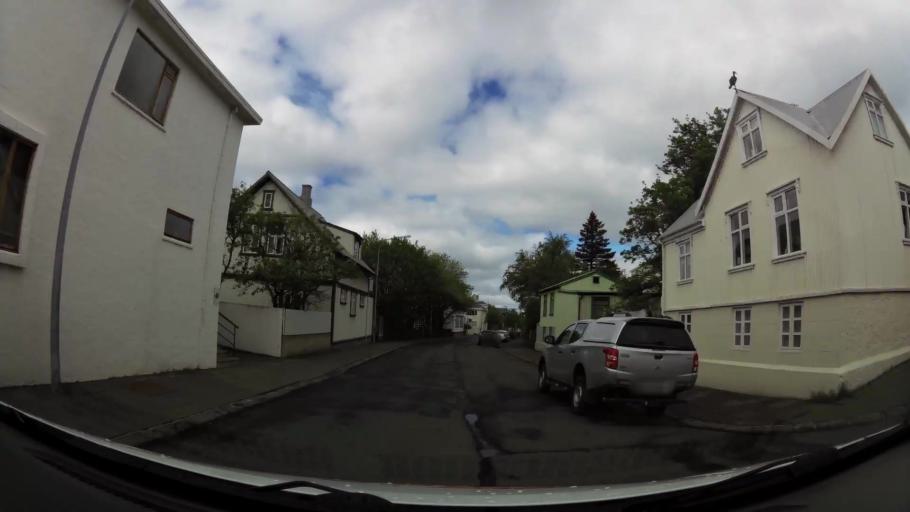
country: IS
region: Capital Region
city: Kopavogur
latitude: 64.1420
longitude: -21.9373
